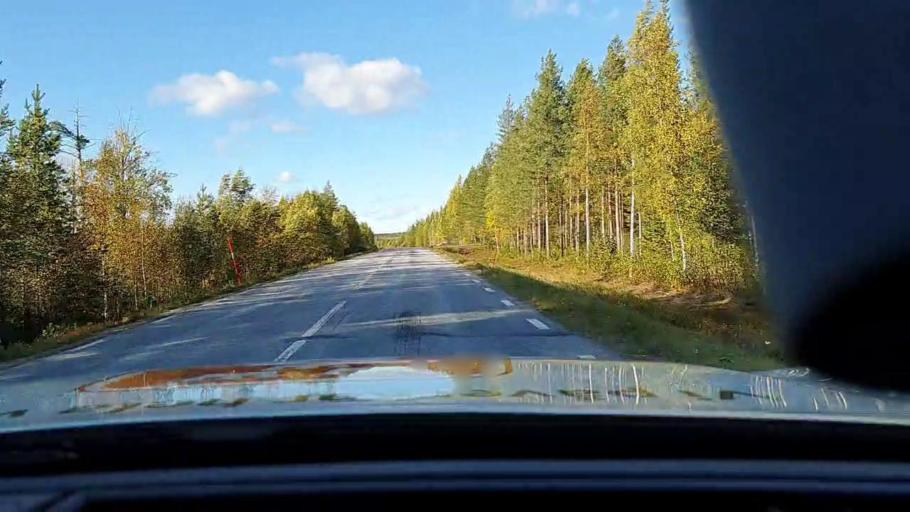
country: SE
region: Norrbotten
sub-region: Pitea Kommun
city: Norrfjarden
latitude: 65.4540
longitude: 21.4561
